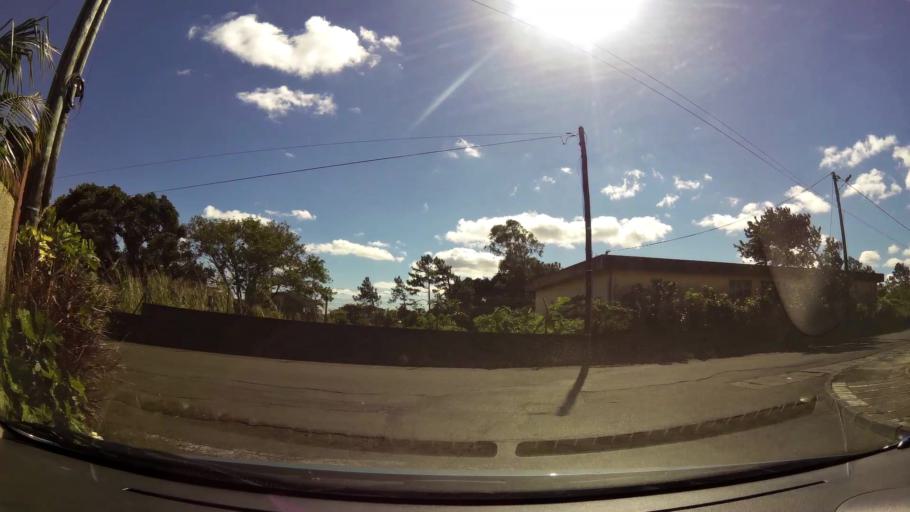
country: MU
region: Plaines Wilhems
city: Vacoas
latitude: -20.3284
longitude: 57.4850
